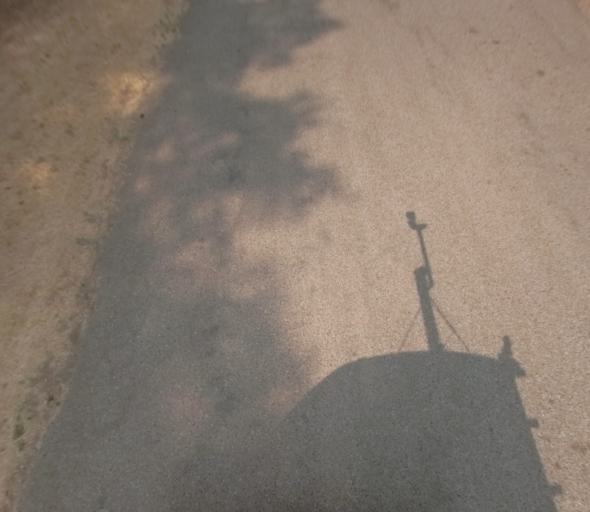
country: US
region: California
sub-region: Madera County
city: Coarsegold
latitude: 37.2195
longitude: -119.6770
